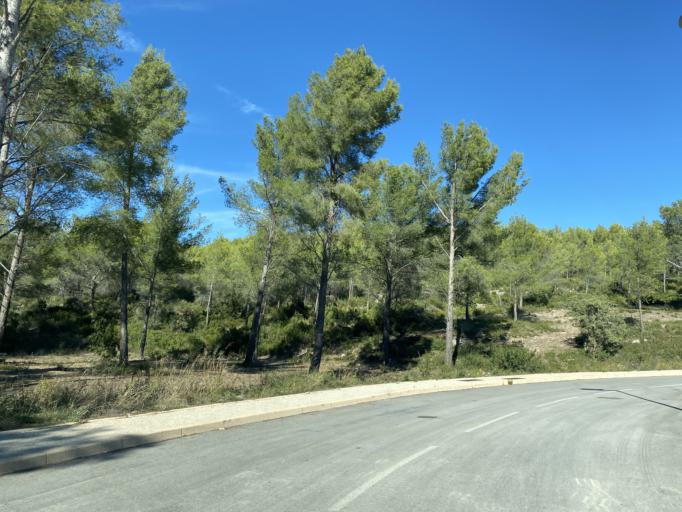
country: FR
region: Provence-Alpes-Cote d'Azur
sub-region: Departement des Bouches-du-Rhone
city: Ceyreste
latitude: 43.2143
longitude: 5.6002
